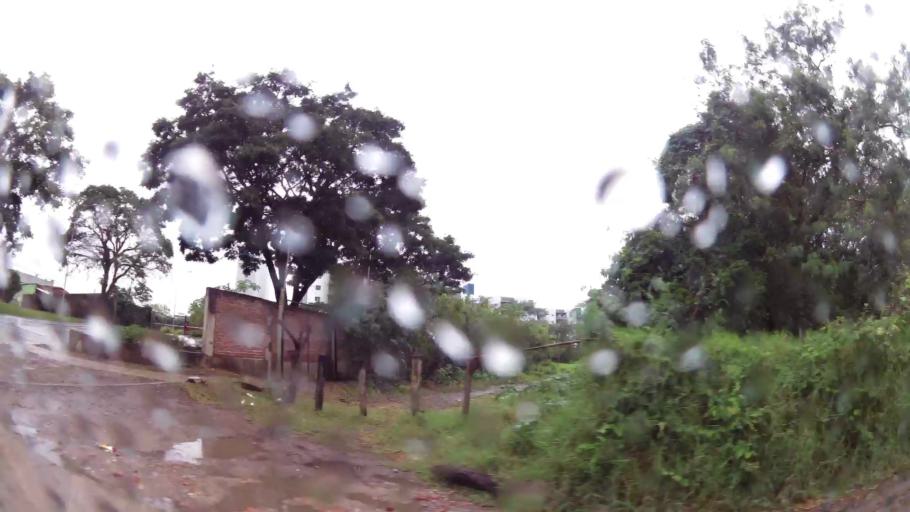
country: BO
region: Santa Cruz
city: Santa Cruz de la Sierra
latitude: -17.7926
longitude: -63.2216
